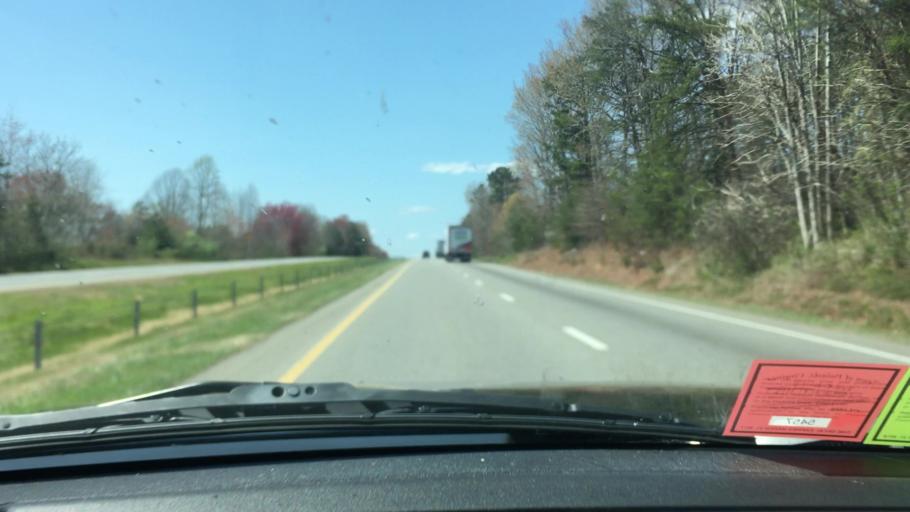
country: US
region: North Carolina
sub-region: Surry County
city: Pilot Mountain
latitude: 36.4158
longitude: -80.5083
